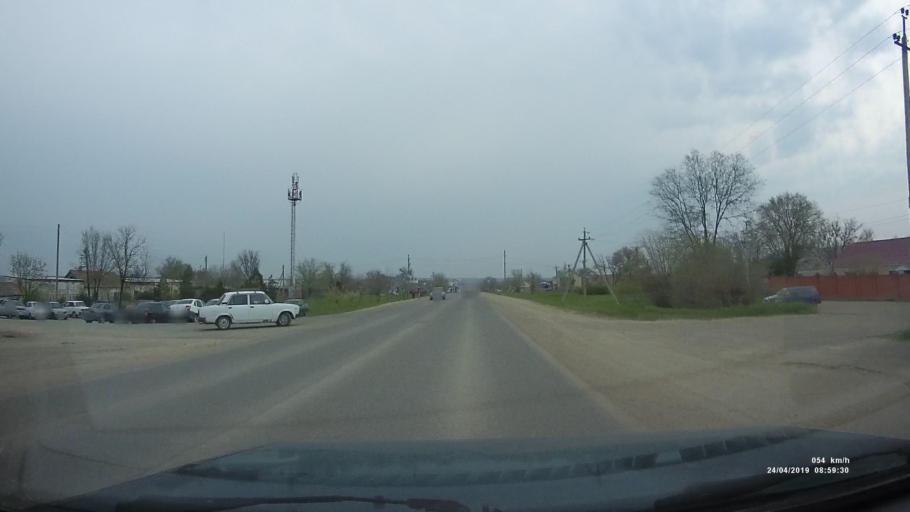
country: RU
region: Kalmykiya
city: Arshan'
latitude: 46.3127
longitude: 44.2104
